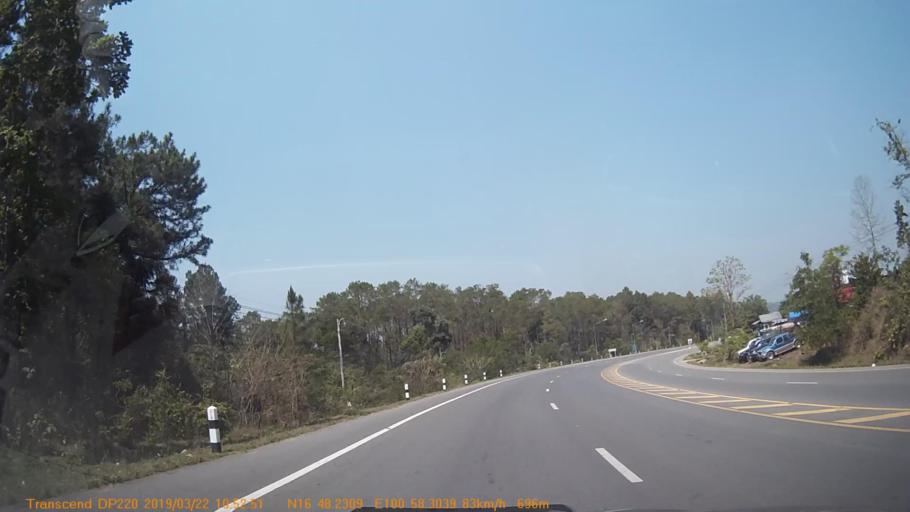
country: TH
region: Phetchabun
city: Khao Kho
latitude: 16.8038
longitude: 100.9715
